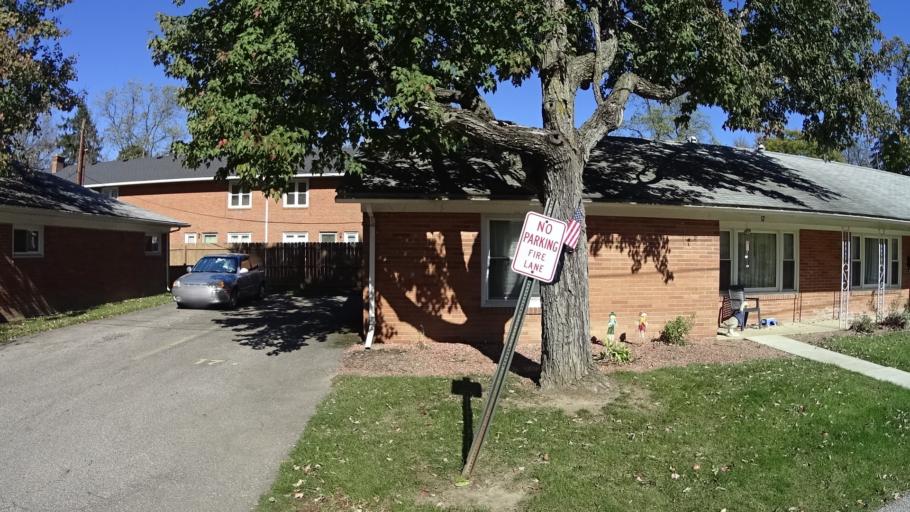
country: US
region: Ohio
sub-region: Lorain County
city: Oberlin
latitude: 41.2904
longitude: -82.2093
